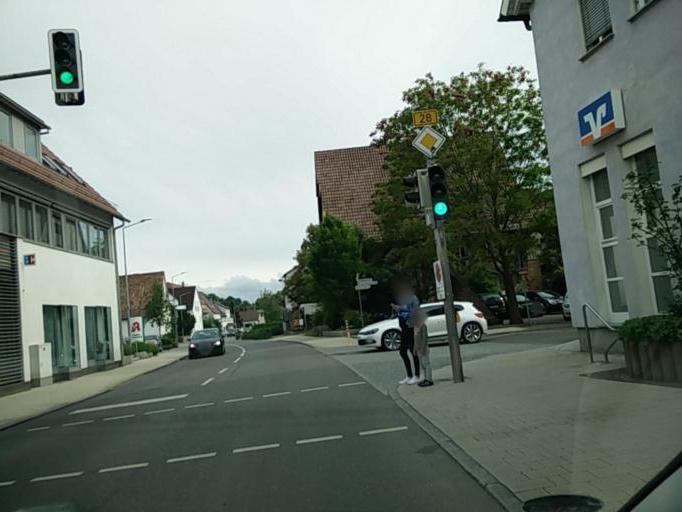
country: DE
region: Baden-Wuerttemberg
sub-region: Regierungsbezirk Stuttgart
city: Hildrizhausen
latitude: 48.5541
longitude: 8.9657
